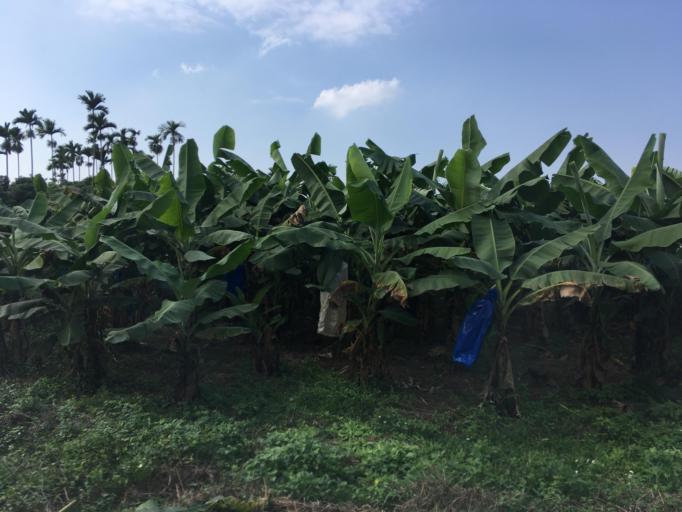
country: TW
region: Taiwan
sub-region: Chiayi
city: Jiayi Shi
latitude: 23.4939
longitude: 120.5221
